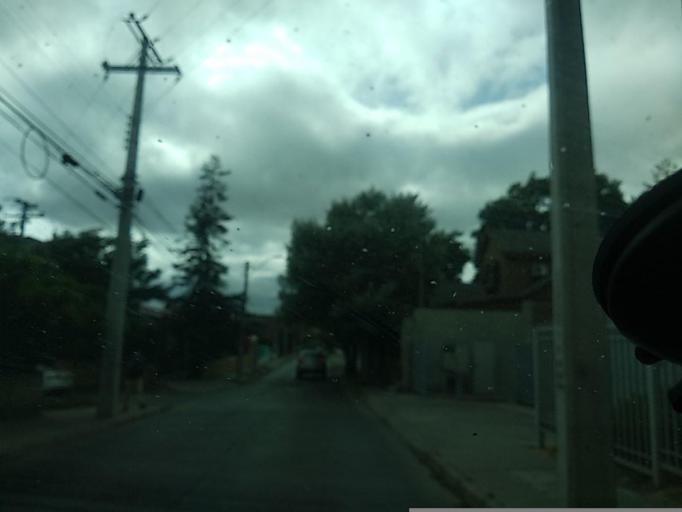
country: CL
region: Valparaiso
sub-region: Provincia de Marga Marga
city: Quilpue
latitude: -33.0489
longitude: -71.4473
